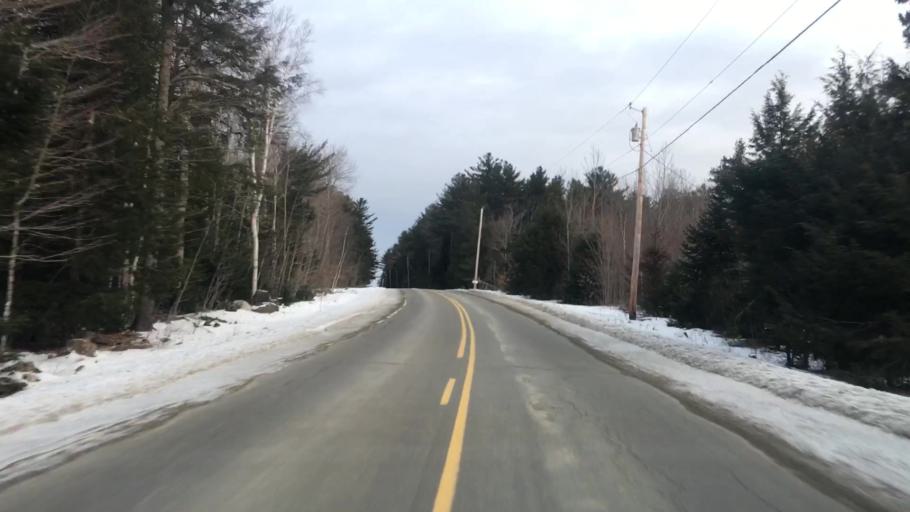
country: US
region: Maine
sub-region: Hancock County
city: Franklin
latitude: 44.7627
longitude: -68.3250
